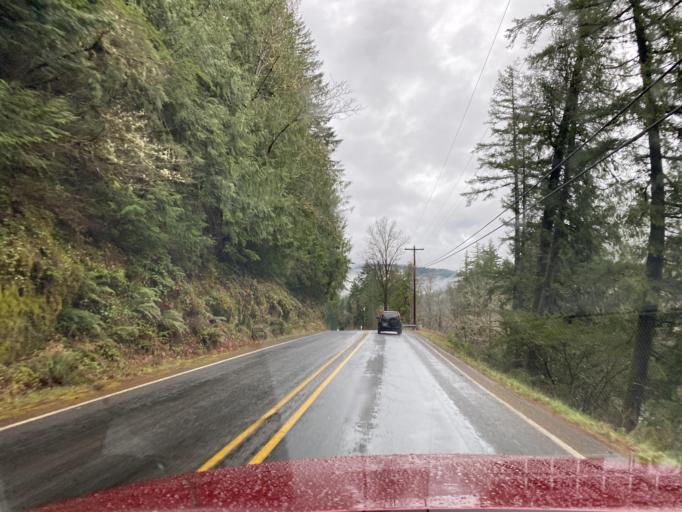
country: US
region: Oregon
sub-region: Lane County
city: Oakridge
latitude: 43.7567
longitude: -122.5099
